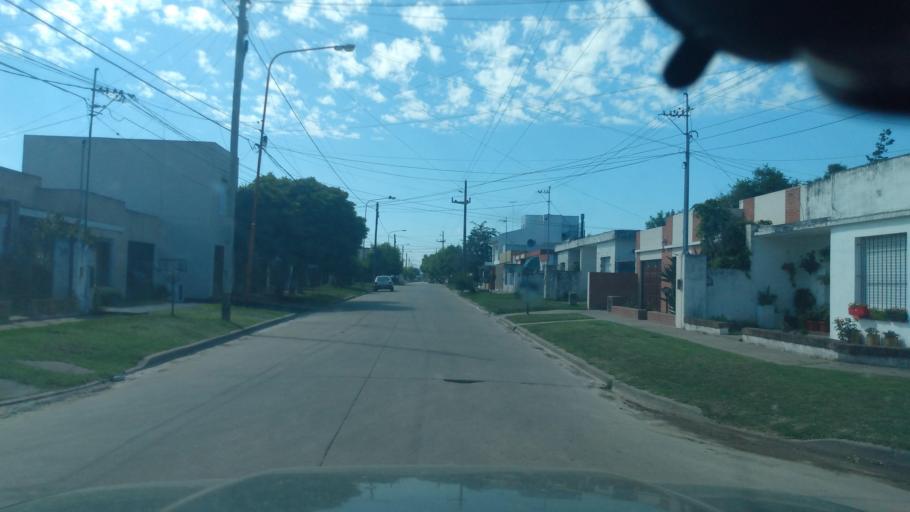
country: AR
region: Buenos Aires
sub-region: Partido de Lujan
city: Lujan
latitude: -34.5755
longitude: -59.1256
